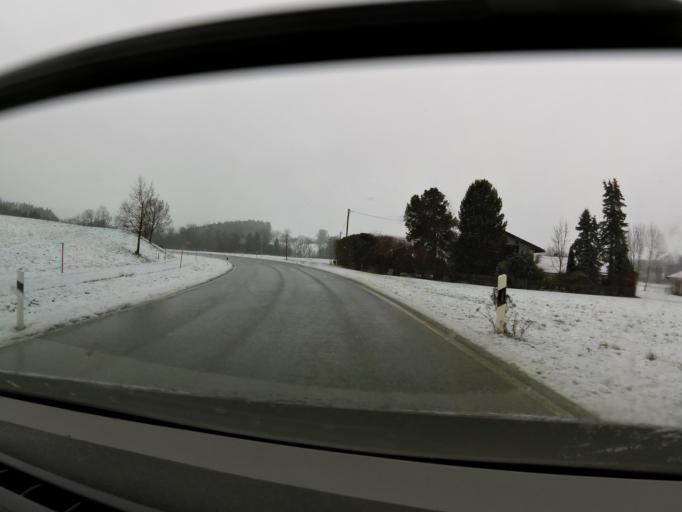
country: DE
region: Bavaria
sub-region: Upper Bavaria
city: Gmund am Tegernsee
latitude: 47.7564
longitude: 11.7112
